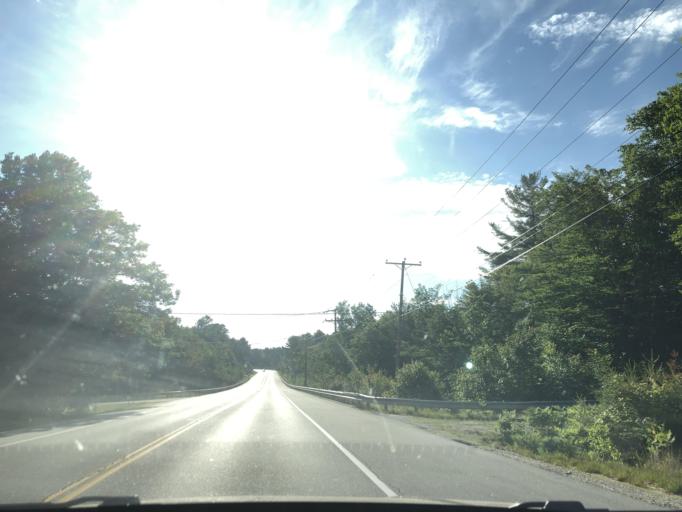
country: US
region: New Hampshire
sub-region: Merrimack County
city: New London
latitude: 43.3939
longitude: -71.9744
